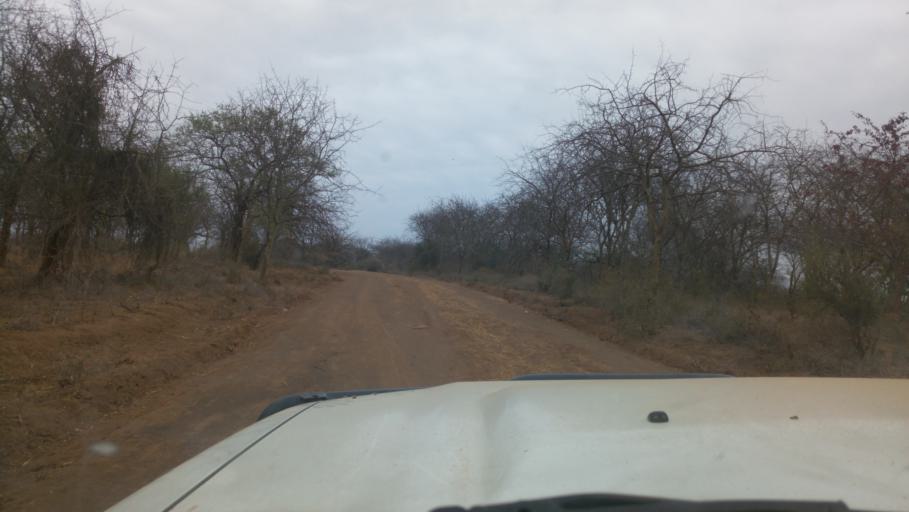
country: KE
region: Makueni
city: Wote
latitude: -1.9624
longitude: 38.1077
